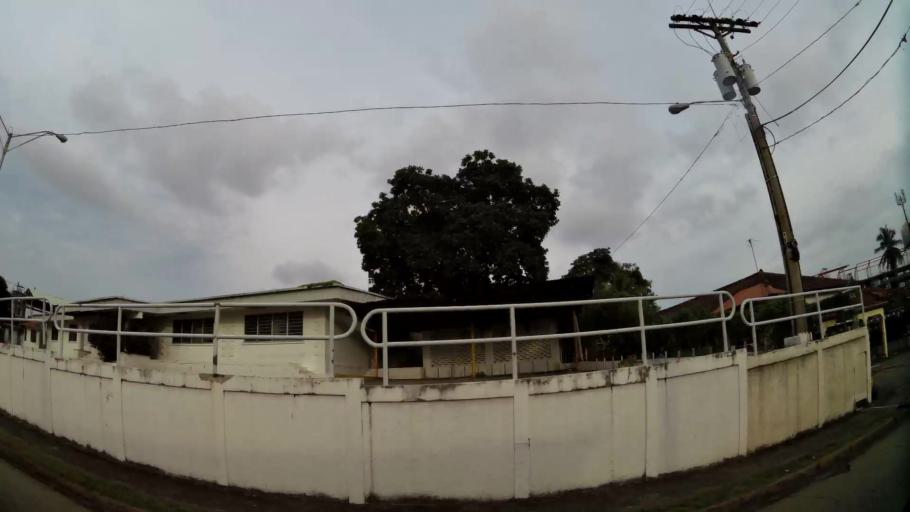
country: PA
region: Panama
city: Panama
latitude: 8.9949
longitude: -79.5167
